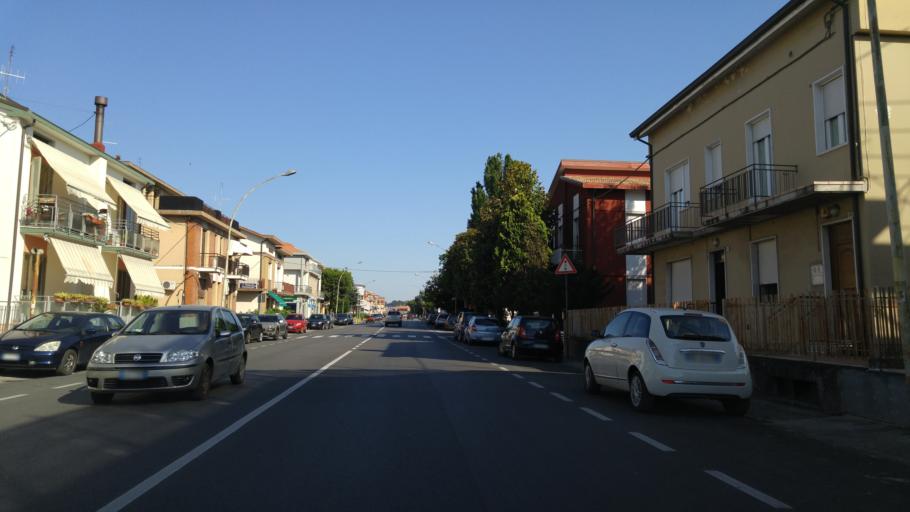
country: IT
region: The Marches
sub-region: Provincia di Pesaro e Urbino
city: Pesaro
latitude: 43.9004
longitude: 12.8964
